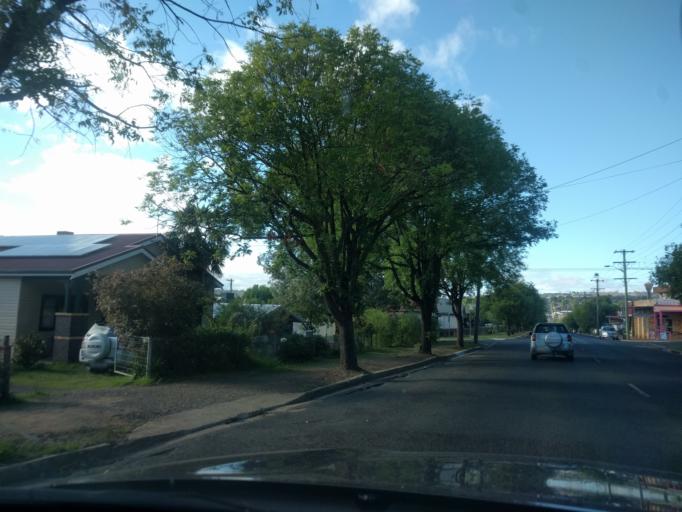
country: AU
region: New South Wales
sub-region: Armidale Dumaresq
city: Armidale
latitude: -30.5063
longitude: 151.6719
